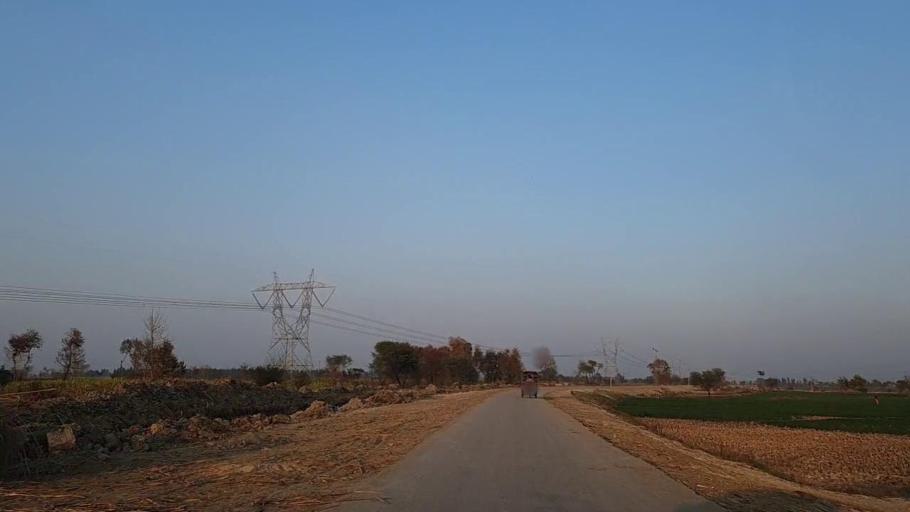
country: PK
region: Sindh
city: Naushahro Firoz
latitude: 26.7656
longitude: 68.0456
